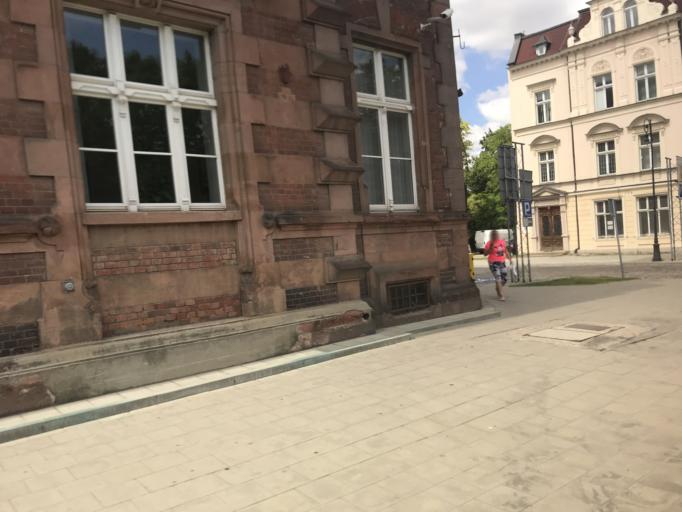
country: PL
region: Warmian-Masurian Voivodeship
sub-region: Powiat elblaski
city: Elblag
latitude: 54.1604
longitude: 19.3984
